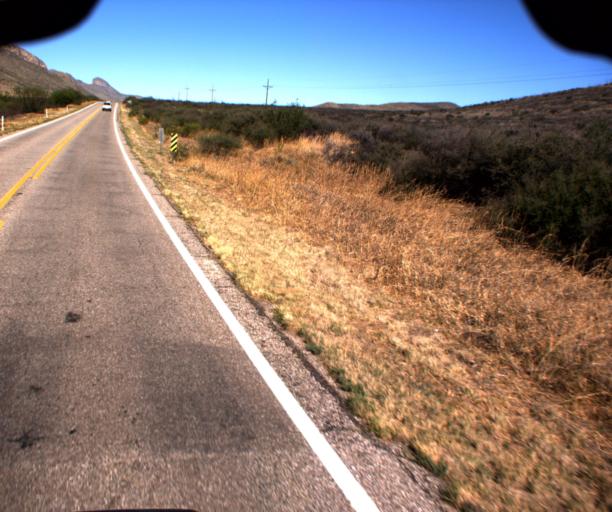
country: US
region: Arizona
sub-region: Cochise County
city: Huachuca City
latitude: 31.6920
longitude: -110.4026
